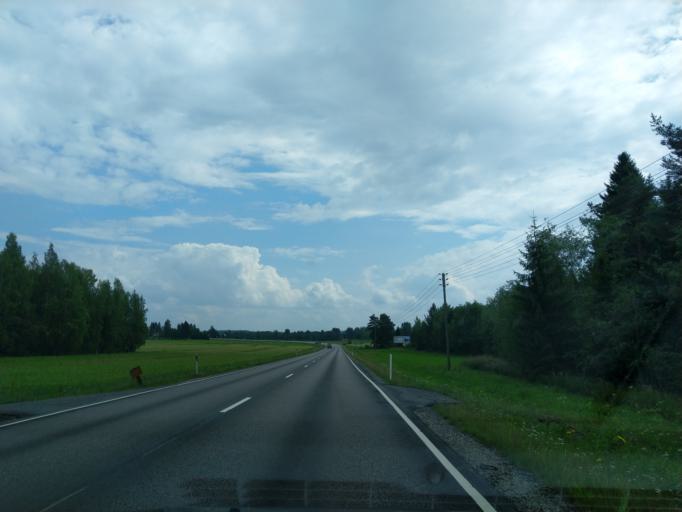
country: FI
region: South Karelia
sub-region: Imatra
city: Parikkala
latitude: 61.6079
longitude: 29.4596
